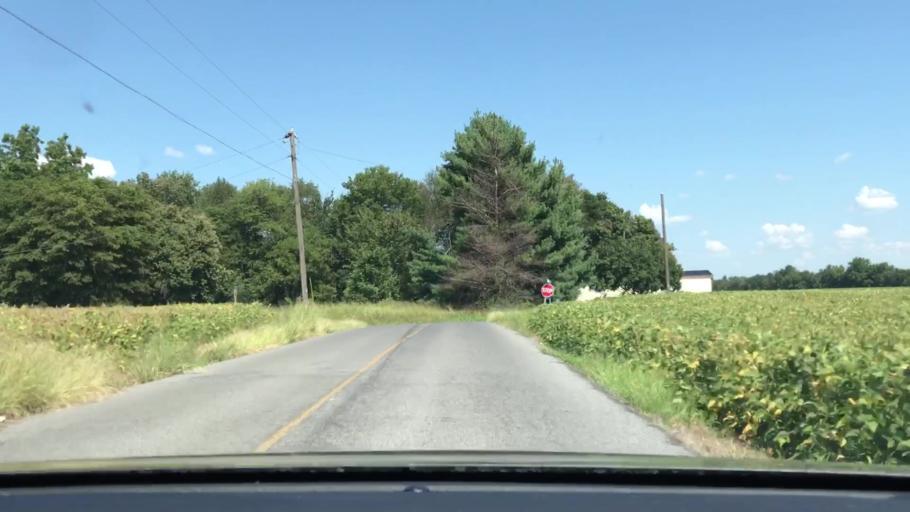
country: US
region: Kentucky
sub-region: Fulton County
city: Fulton
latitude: 36.5219
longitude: -88.9014
